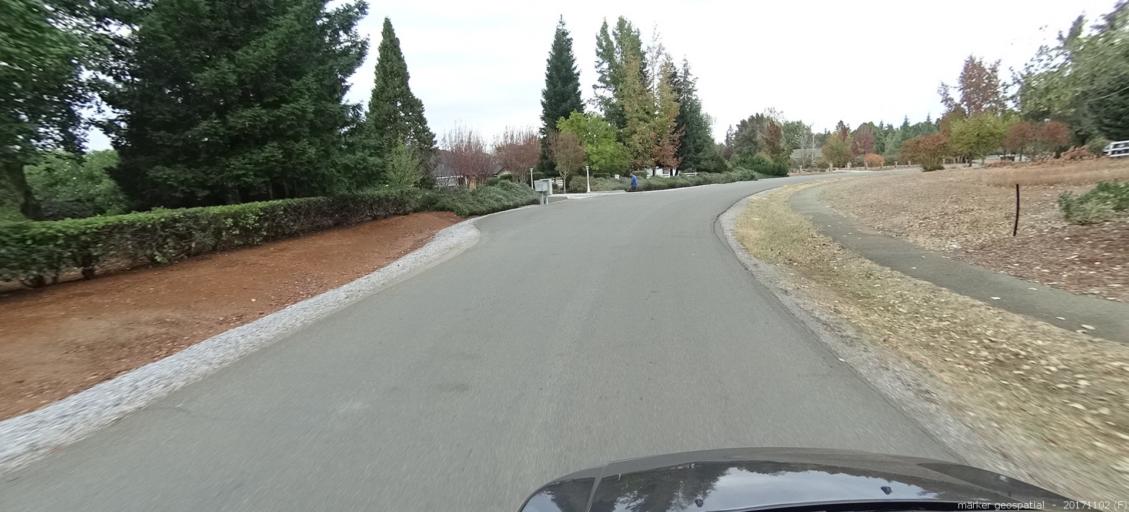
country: US
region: California
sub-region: Shasta County
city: Shasta Lake
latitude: 40.6533
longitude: -122.3235
